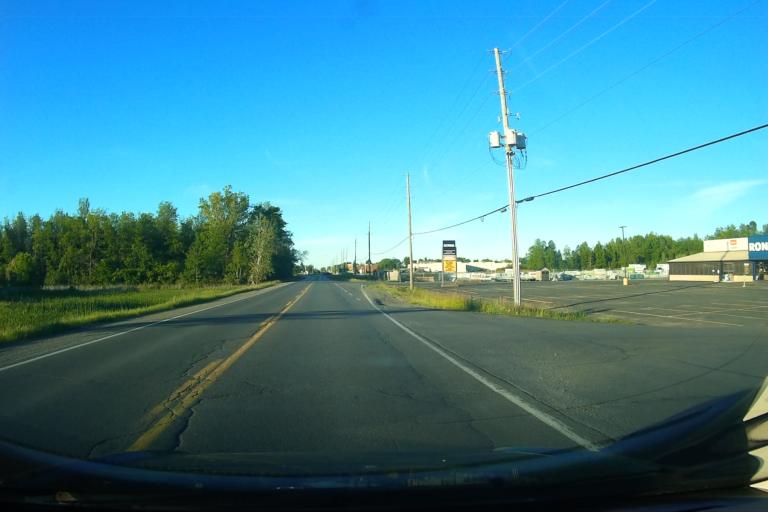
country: CA
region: Ontario
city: Prescott
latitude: 45.0169
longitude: -75.6616
